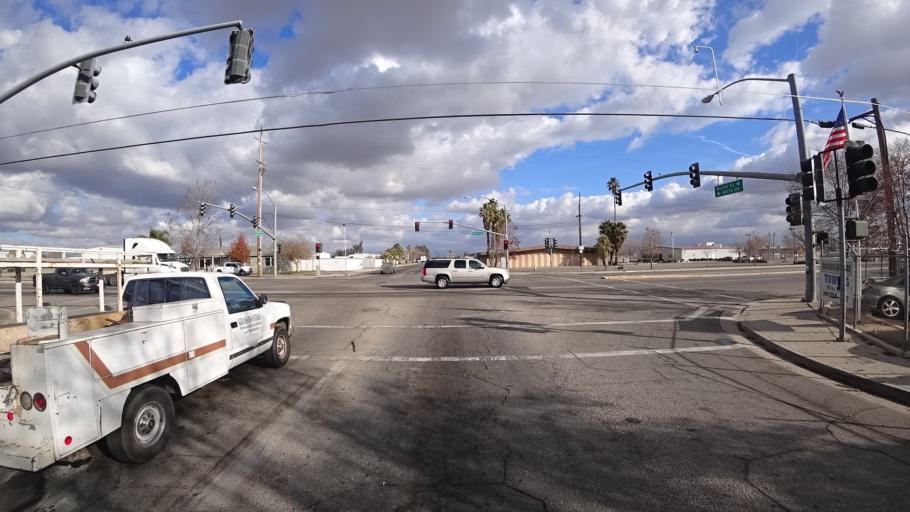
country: US
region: California
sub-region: Kern County
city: Bakersfield
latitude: 35.3322
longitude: -119.0033
